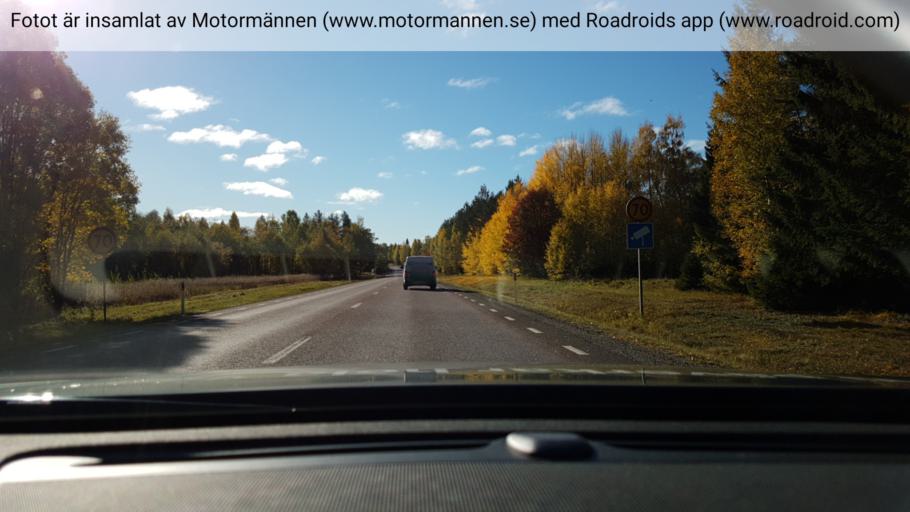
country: SE
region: Vaesterbotten
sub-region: Skelleftea Kommun
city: Burea
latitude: 64.6229
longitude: 21.1786
